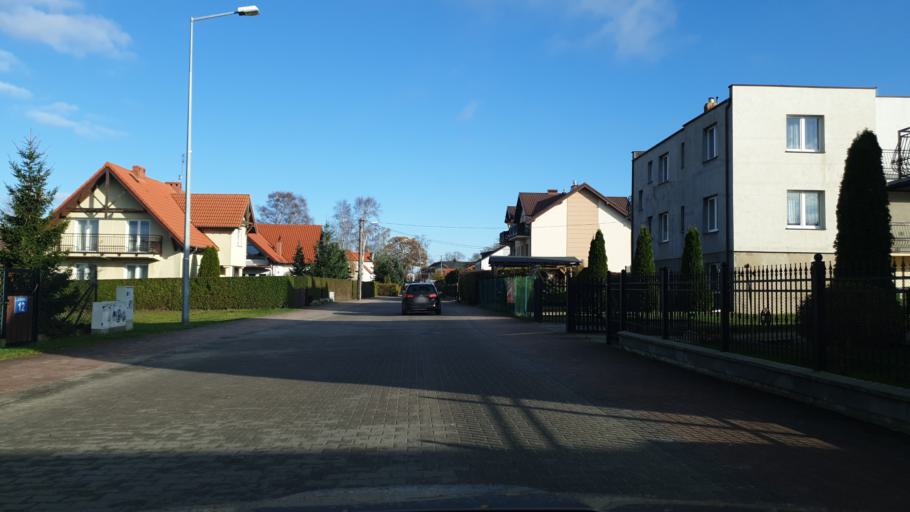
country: PL
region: Pomeranian Voivodeship
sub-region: Powiat pucki
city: Jastrzebia Gora
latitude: 54.8235
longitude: 18.2402
